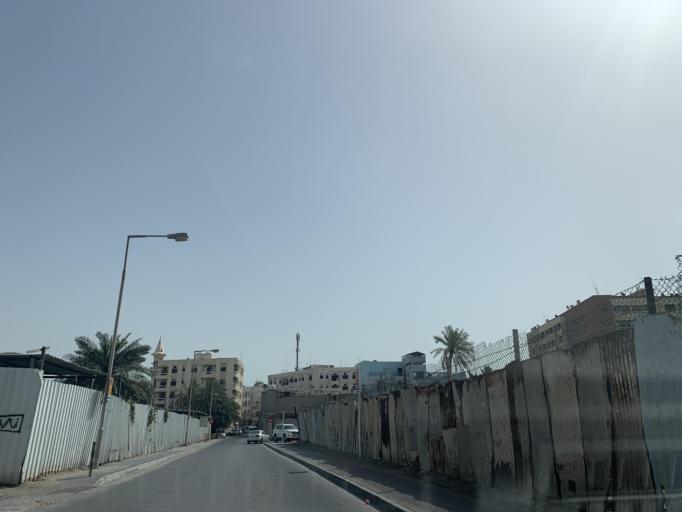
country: BH
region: Manama
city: Manama
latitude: 26.2246
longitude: 50.5687
